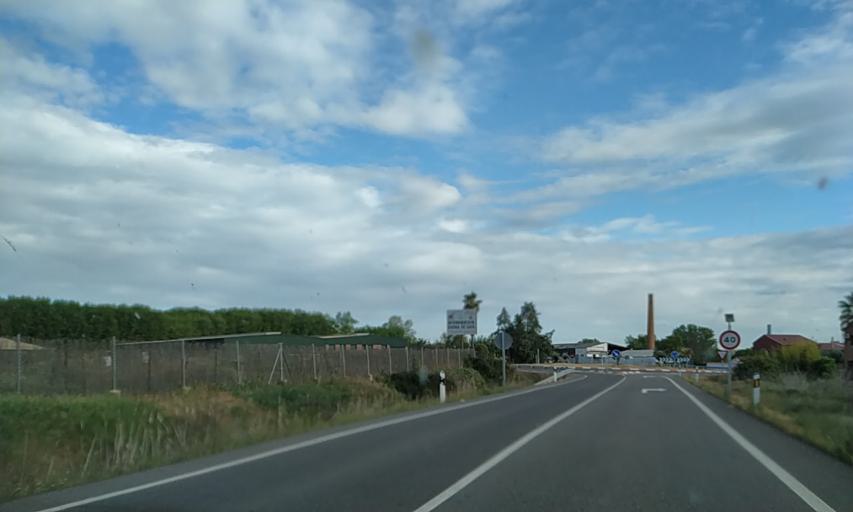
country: ES
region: Extremadura
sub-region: Provincia de Caceres
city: Moraleja
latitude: 40.0787
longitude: -6.6688
